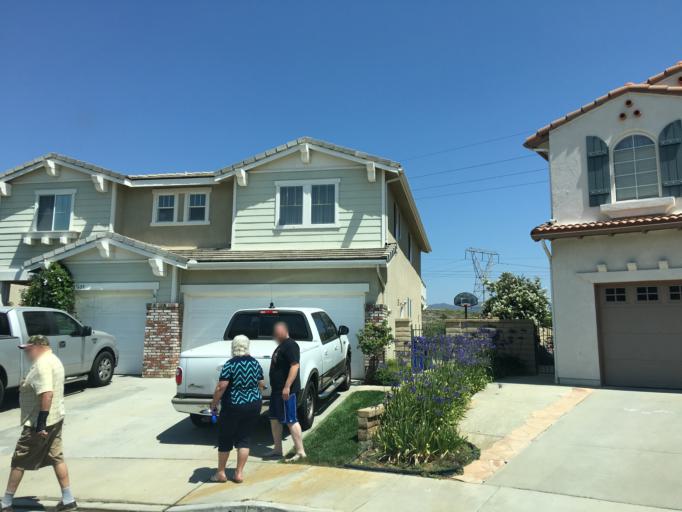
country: US
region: California
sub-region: Los Angeles County
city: Castaic
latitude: 34.5053
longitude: -118.6207
